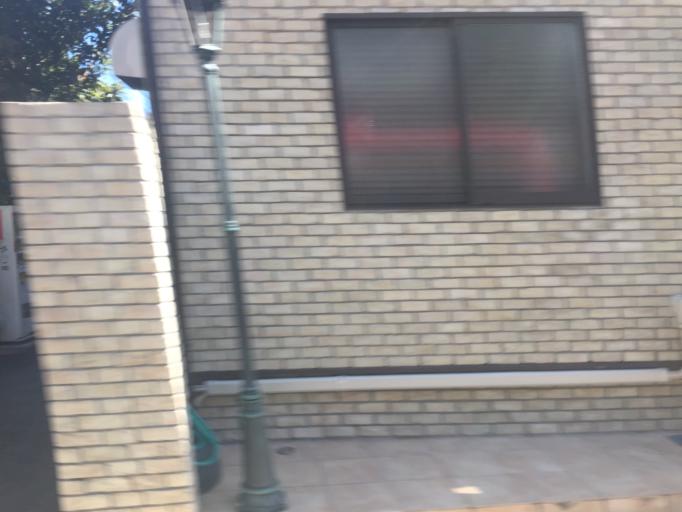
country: JP
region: Tokyo
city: Tokyo
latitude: 35.6533
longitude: 139.6986
